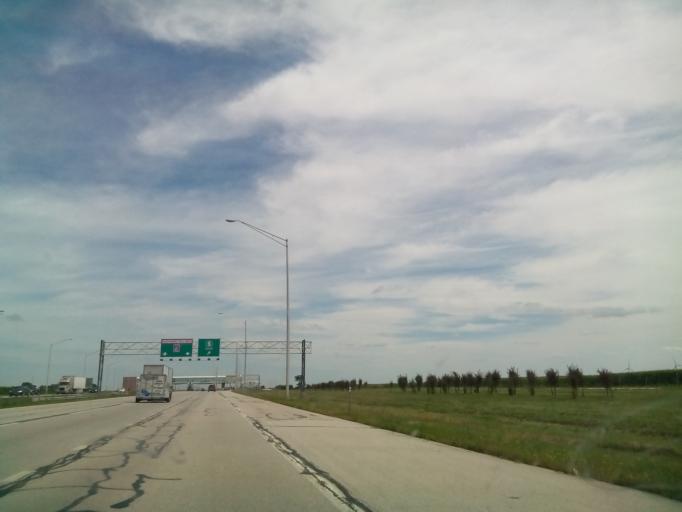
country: US
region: Illinois
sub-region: DeKalb County
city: Malta
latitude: 41.8996
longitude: -88.8811
